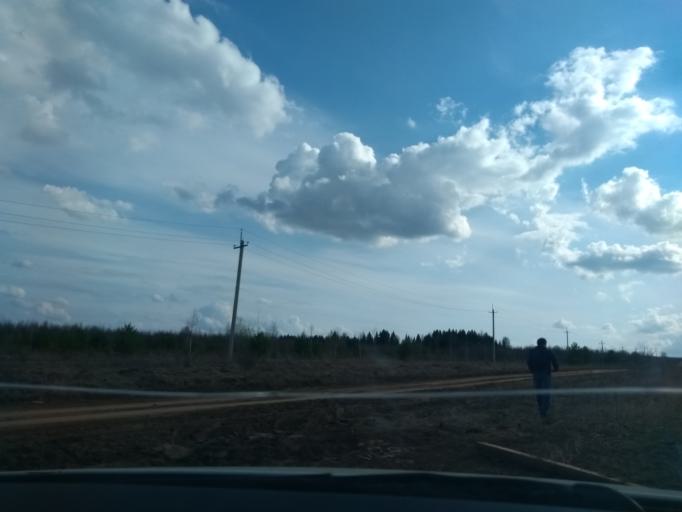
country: RU
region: Perm
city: Sylva
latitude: 57.8406
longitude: 56.7900
